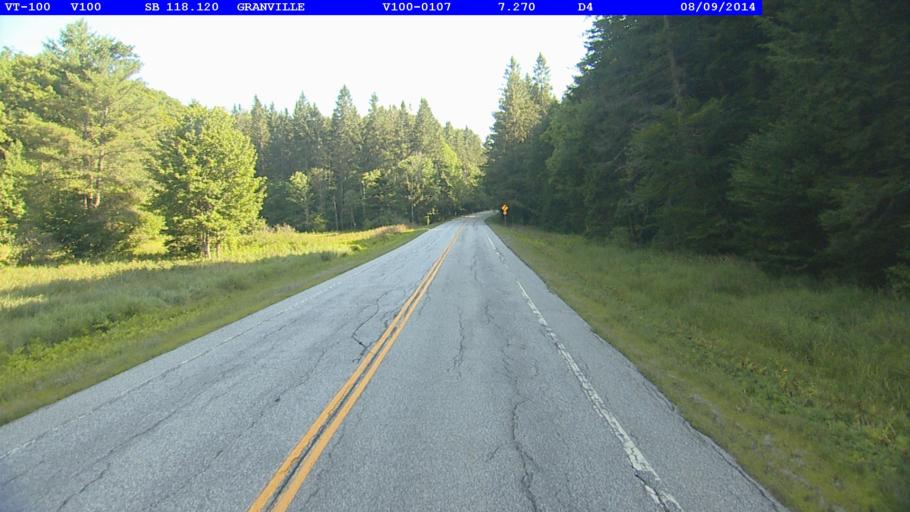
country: US
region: Vermont
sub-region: Orange County
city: Randolph
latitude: 44.0349
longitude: -72.8315
